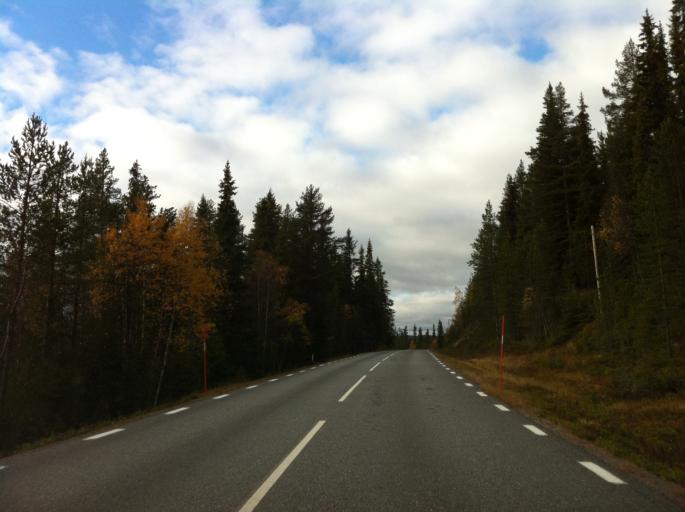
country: NO
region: Hedmark
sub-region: Engerdal
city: Engerdal
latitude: 61.9924
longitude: 12.4586
